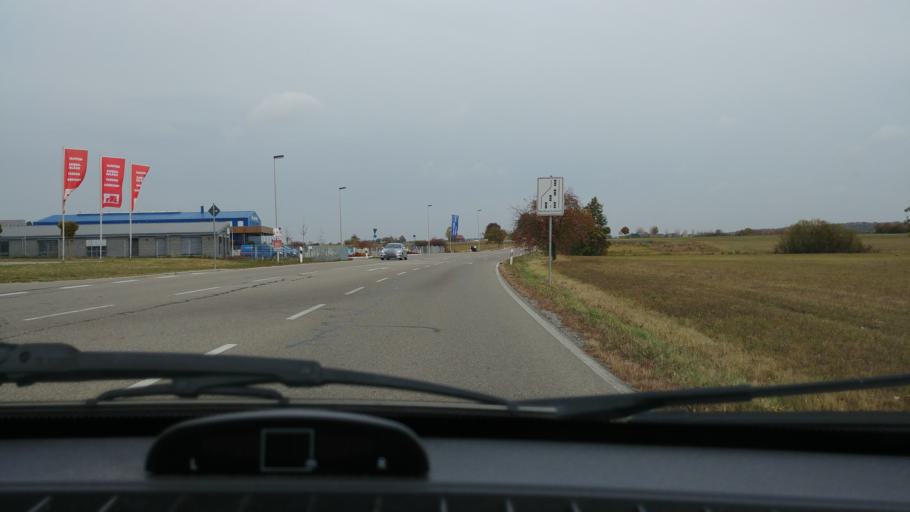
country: DE
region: Baden-Wuerttemberg
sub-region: Regierungsbezirk Stuttgart
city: Crailsheim
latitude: 49.1451
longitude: 10.0342
